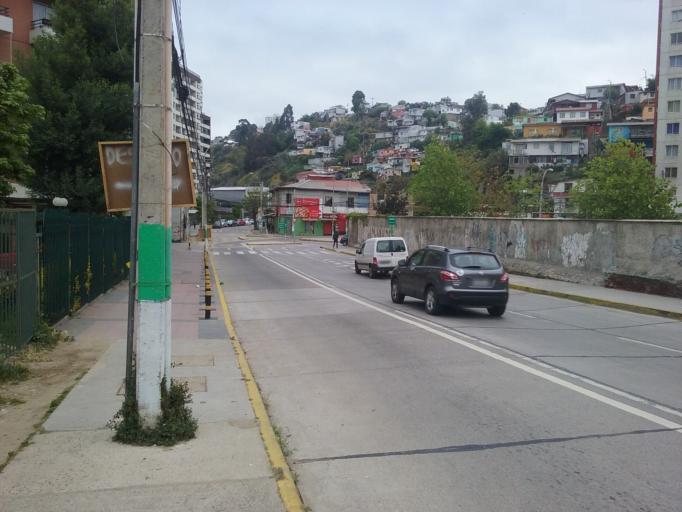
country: CL
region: Valparaiso
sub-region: Provincia de Valparaiso
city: Vina del Mar
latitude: -33.0332
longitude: -71.5888
